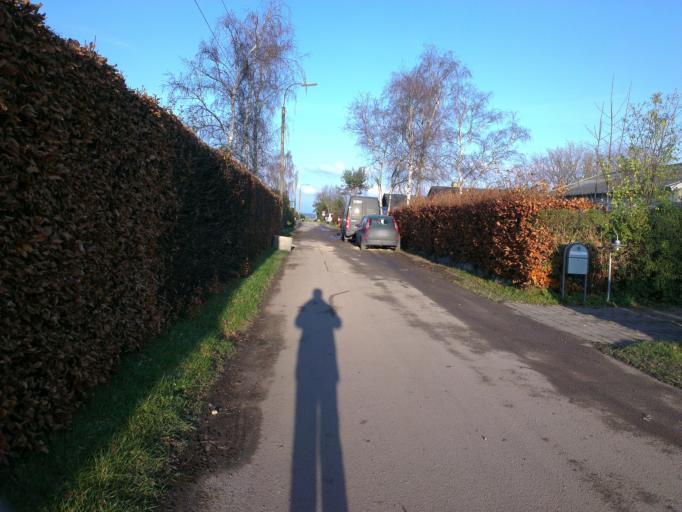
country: DK
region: Capital Region
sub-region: Frederikssund Kommune
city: Jaegerspris
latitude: 55.8575
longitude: 11.9982
